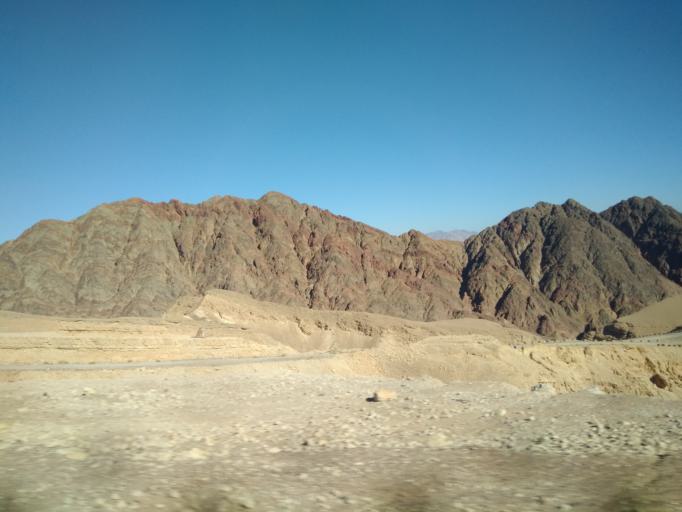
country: IL
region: Southern District
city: Eilat
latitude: 29.5793
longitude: 34.8869
